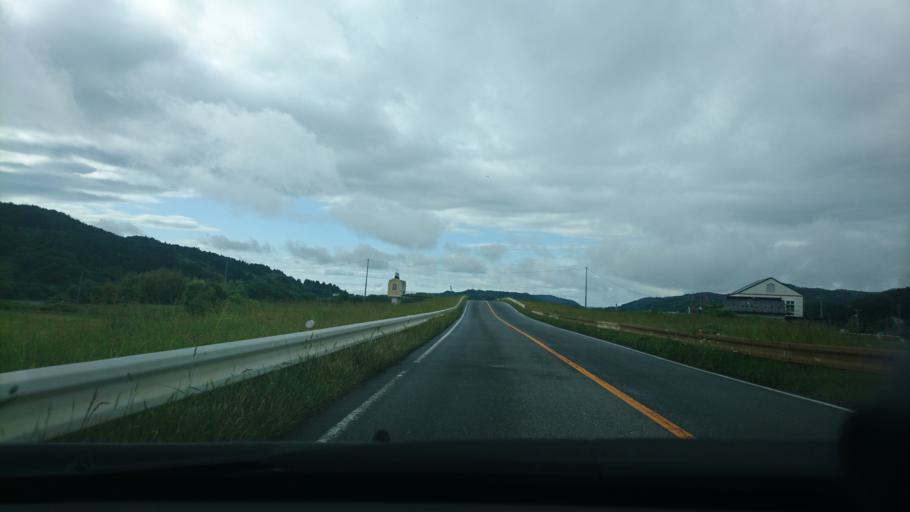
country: JP
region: Miyagi
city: Wakuya
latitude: 38.6388
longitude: 141.2884
